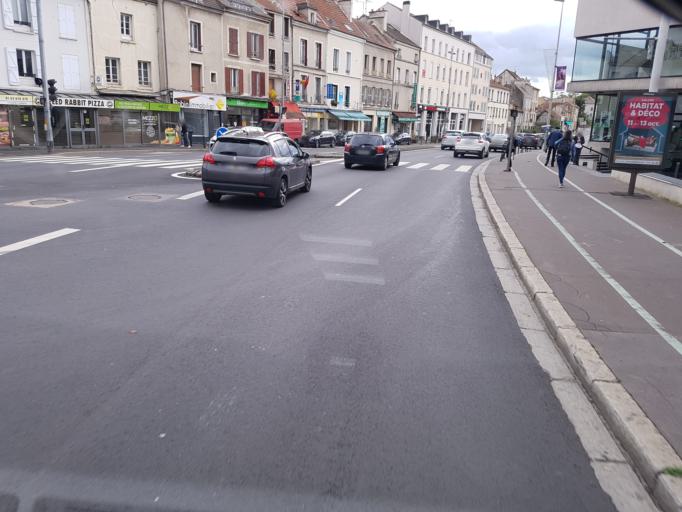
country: FR
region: Ile-de-France
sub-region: Departement de Seine-et-Marne
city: Meaux
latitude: 48.9551
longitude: 2.8790
